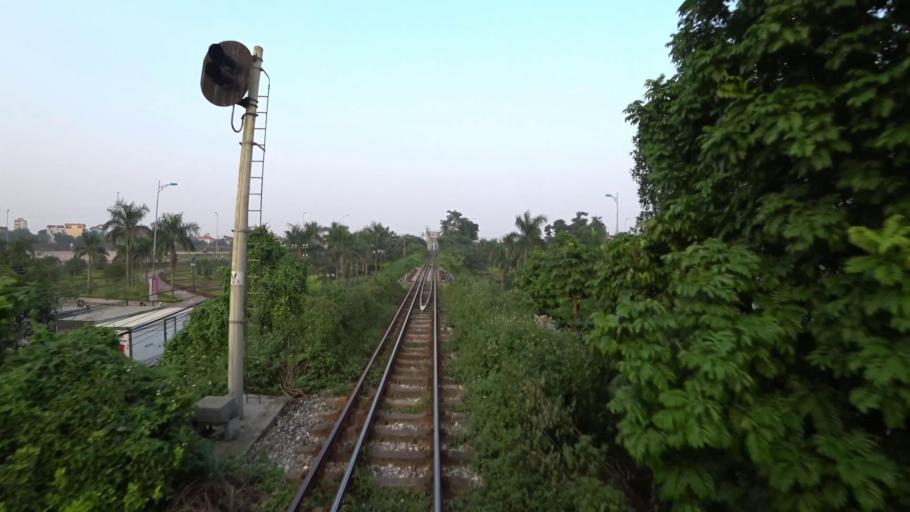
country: VN
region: Ha Noi
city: Trau Quy
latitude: 21.0903
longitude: 105.9195
